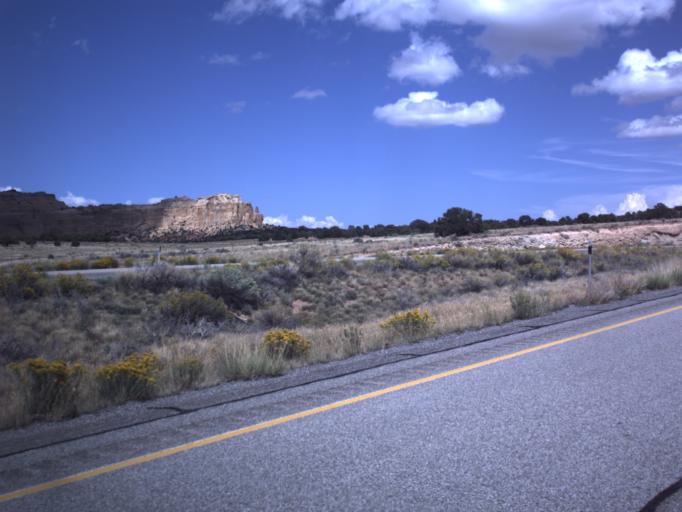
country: US
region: Utah
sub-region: Emery County
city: Castle Dale
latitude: 38.8731
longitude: -110.7577
